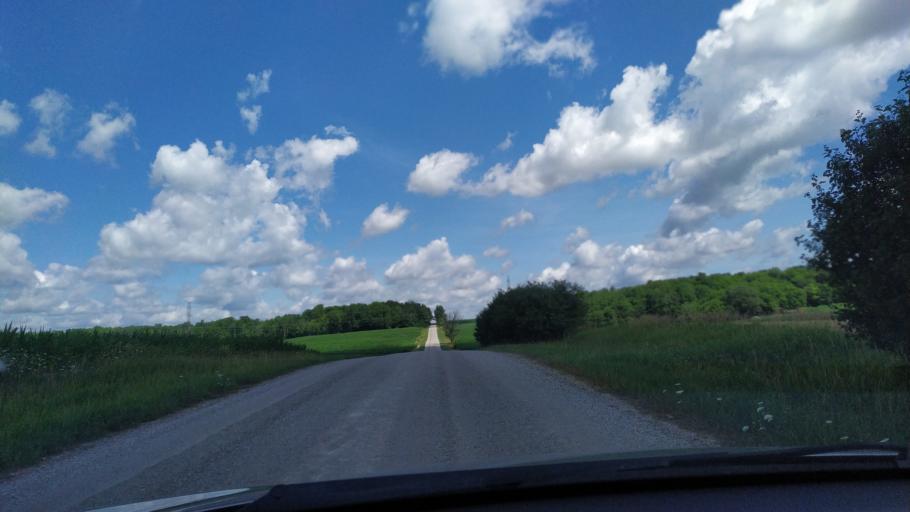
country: CA
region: Ontario
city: Stratford
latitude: 43.3729
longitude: -80.7616
